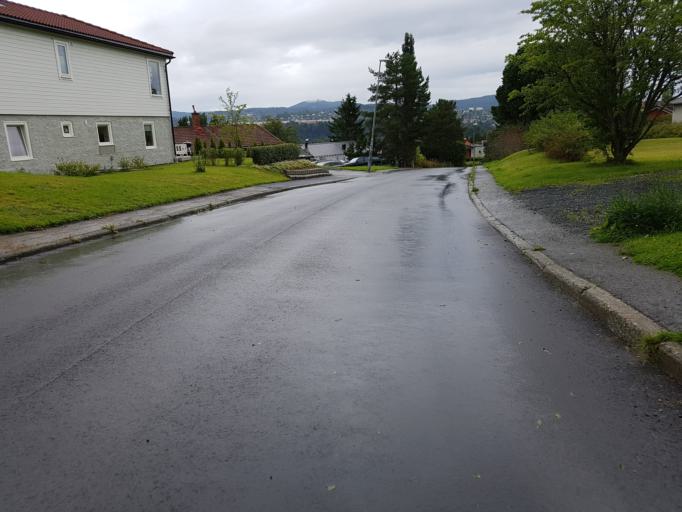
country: NO
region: Sor-Trondelag
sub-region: Trondheim
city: Trondheim
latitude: 63.3884
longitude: 10.4184
